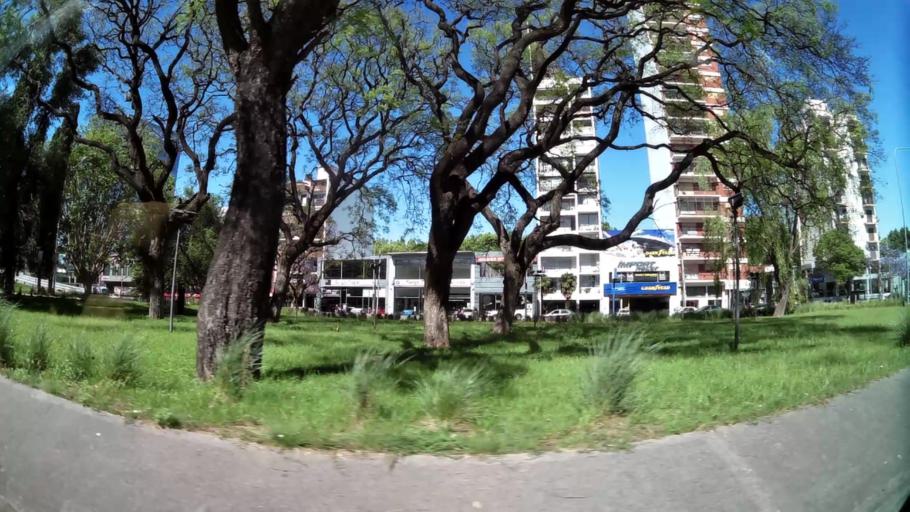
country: AR
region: Buenos Aires
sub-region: Partido de Vicente Lopez
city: Olivos
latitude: -34.5297
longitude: -58.4695
